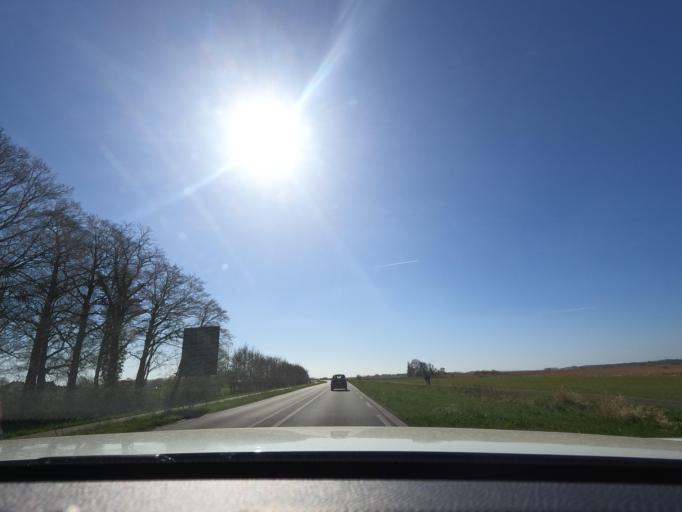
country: NL
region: Gelderland
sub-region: Gemeente Elburg
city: Elburg
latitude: 52.4489
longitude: 5.8265
